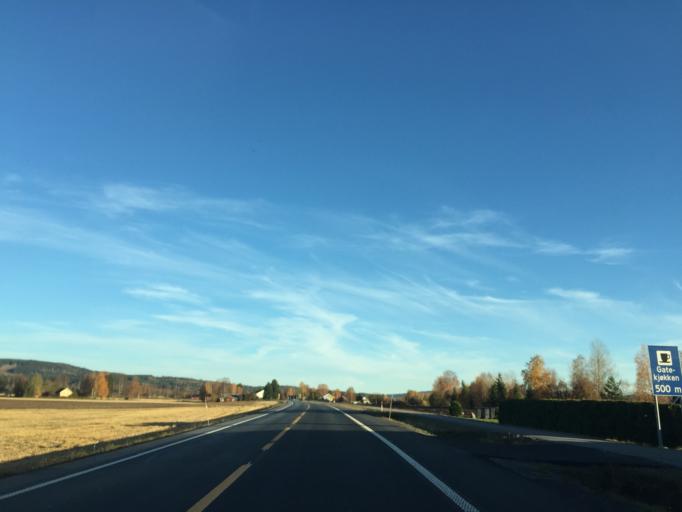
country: NO
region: Hedmark
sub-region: Kongsvinger
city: Spetalen
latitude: 60.2336
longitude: 11.8065
